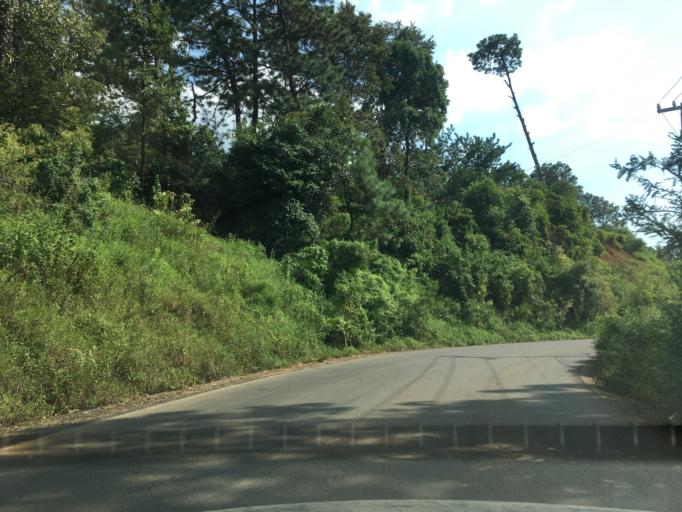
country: MX
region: Michoacan
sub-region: Ziracuaretiro
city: Patuan
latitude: 19.4387
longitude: -101.8876
